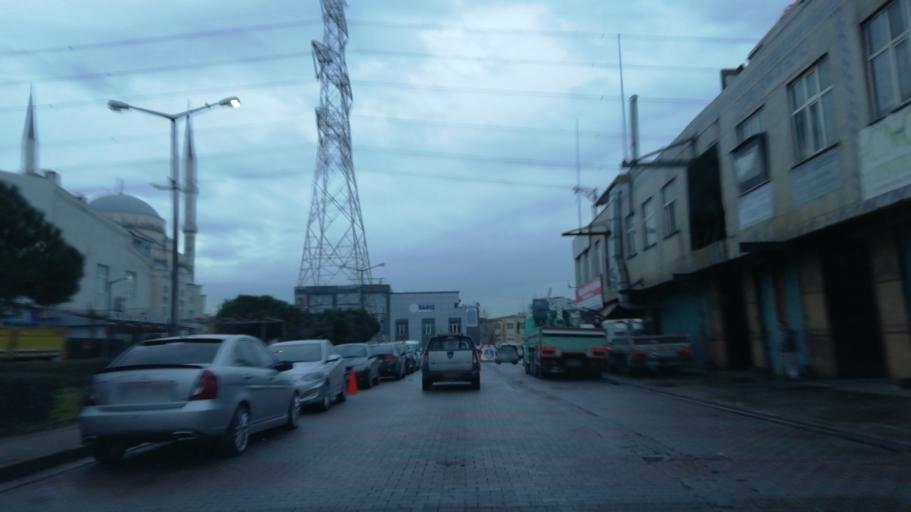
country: TR
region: Istanbul
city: Mahmutbey
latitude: 41.0681
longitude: 28.8065
